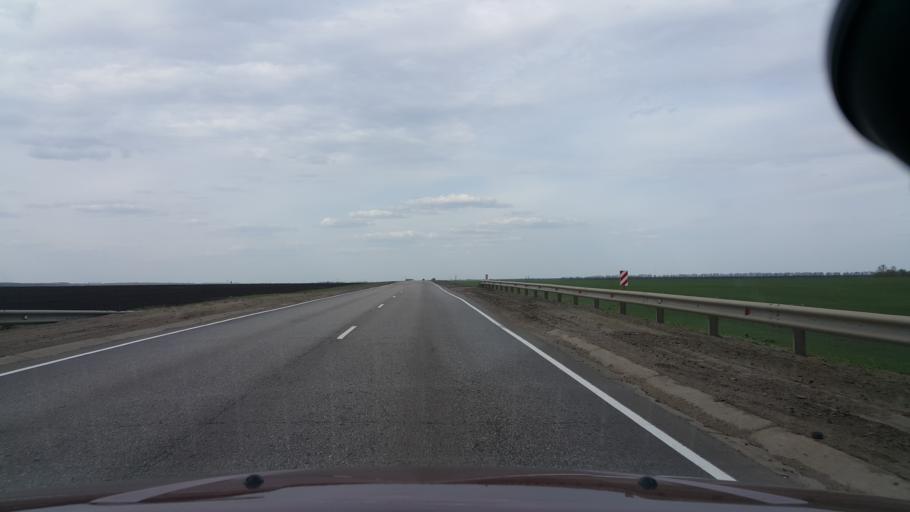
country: RU
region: Tambov
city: Pokrovo-Prigorodnoye
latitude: 52.6165
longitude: 41.3434
